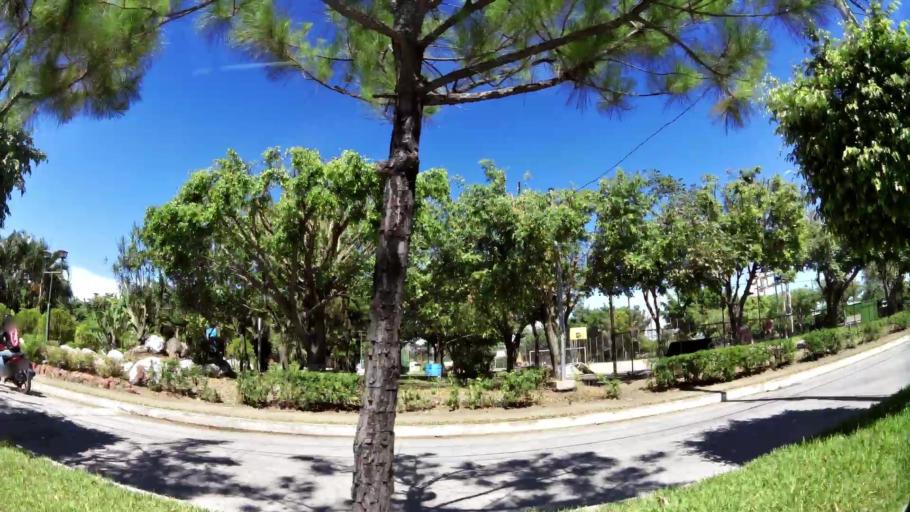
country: SV
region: La Libertad
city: San Juan Opico
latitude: 13.7963
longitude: -89.3580
